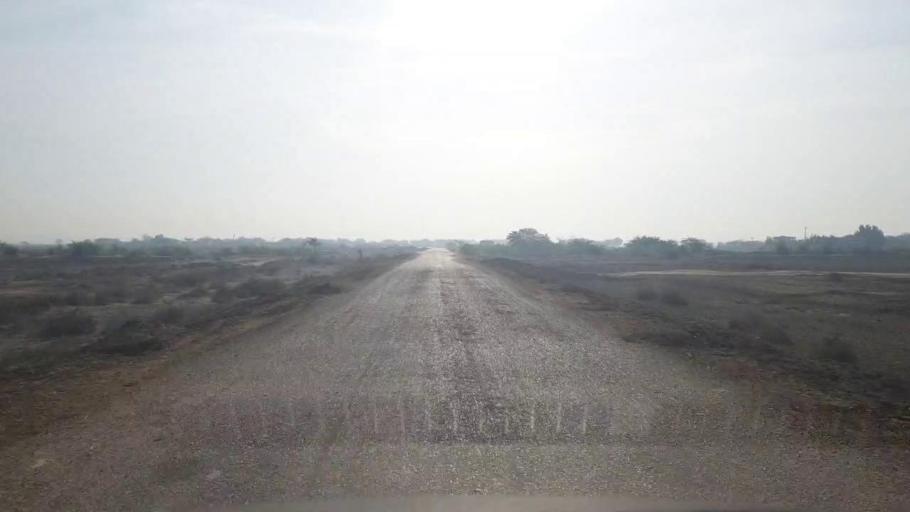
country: PK
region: Sindh
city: Umarkot
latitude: 25.3456
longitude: 69.6983
